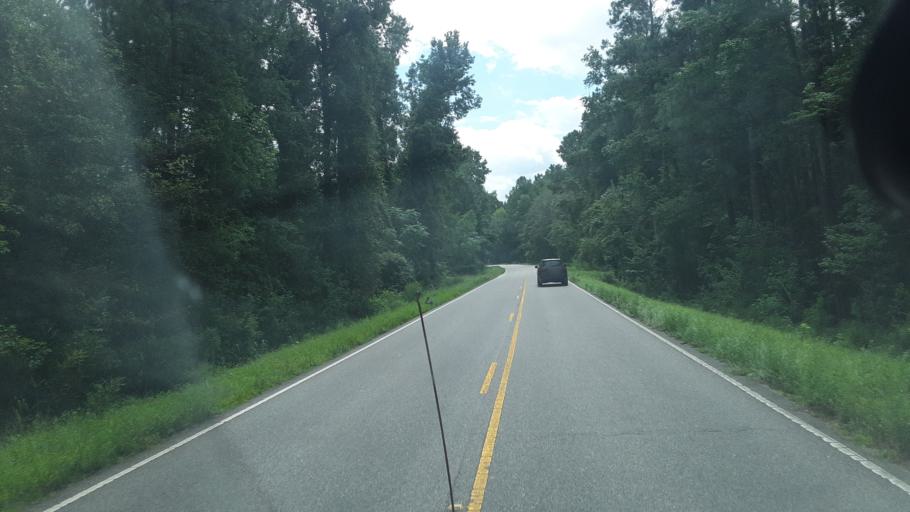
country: US
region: North Carolina
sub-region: Robeson County
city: Fairmont
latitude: 34.3212
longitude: -79.0445
